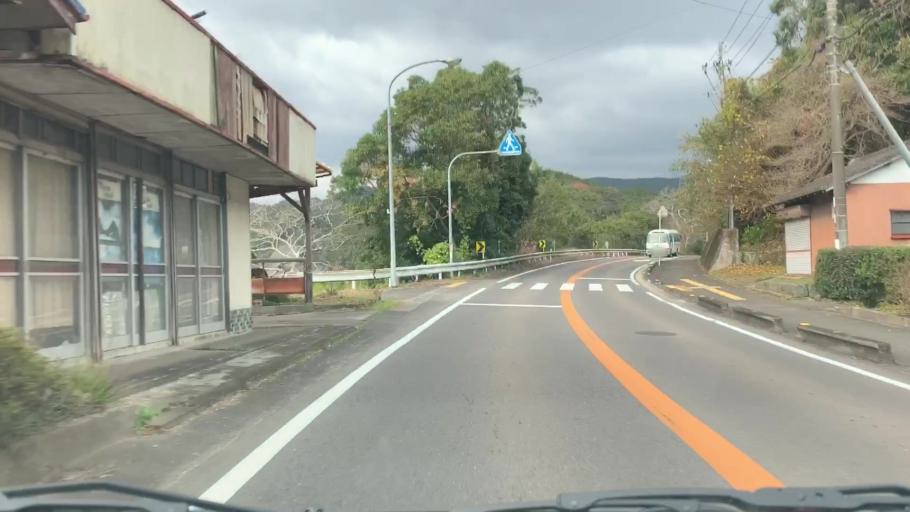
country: JP
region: Saga Prefecture
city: Ureshinomachi-shimojuku
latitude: 33.1316
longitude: 130.0310
